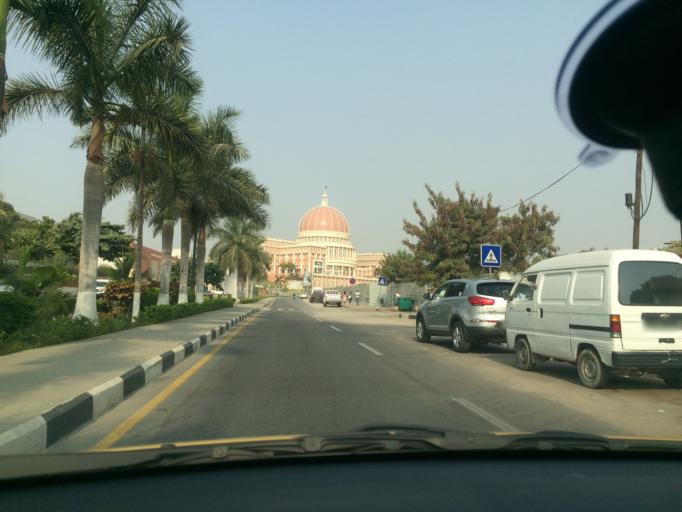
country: AO
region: Luanda
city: Luanda
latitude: -8.8208
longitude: 13.2203
